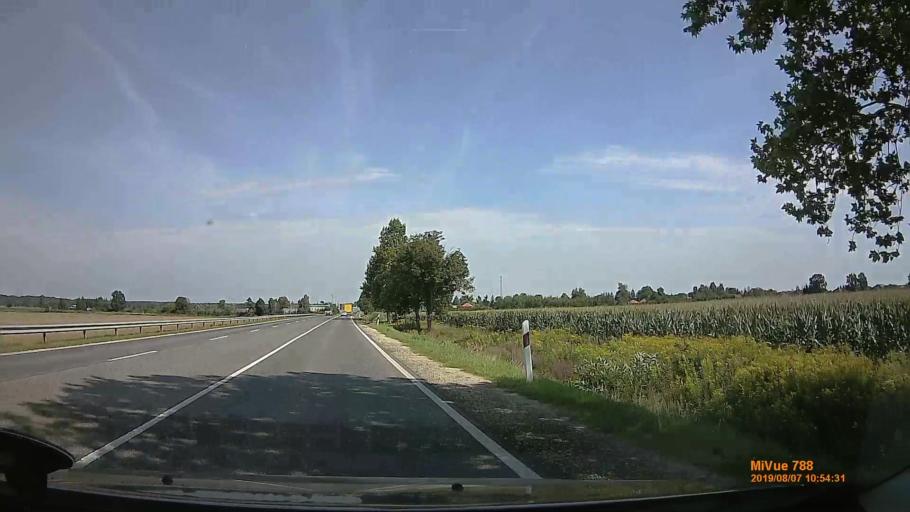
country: SI
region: Lendava-Lendva
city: Lendava
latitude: 46.6109
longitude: 16.4638
